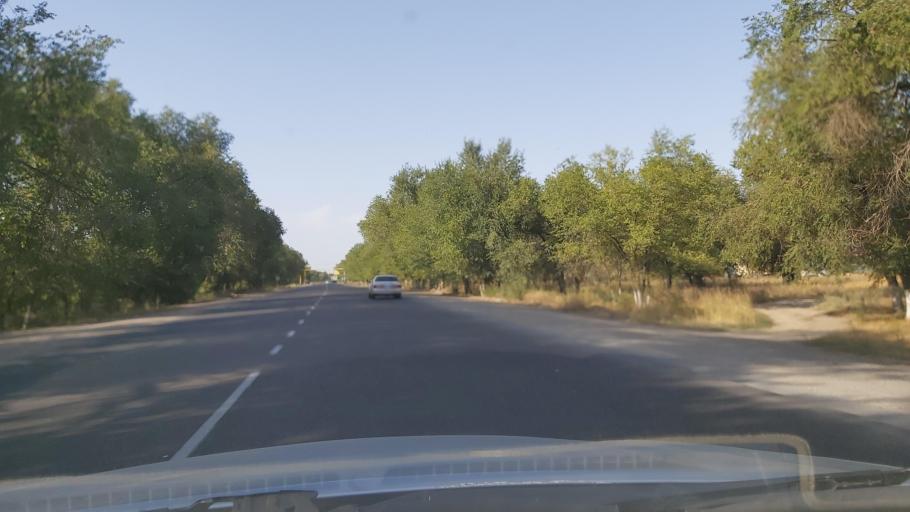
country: KZ
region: Almaty Oblysy
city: Energeticheskiy
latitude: 43.5518
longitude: 77.0529
